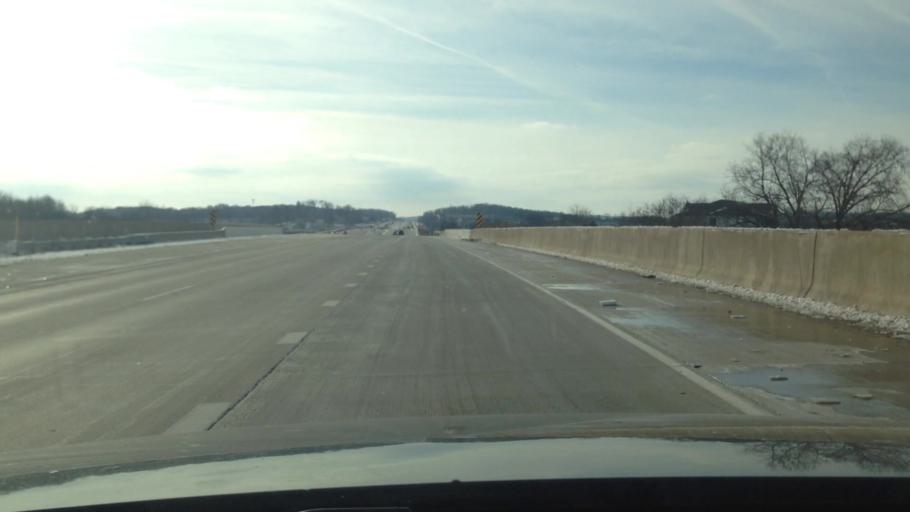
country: US
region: Wisconsin
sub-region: Waukesha County
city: New Berlin
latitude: 42.9564
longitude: -88.1032
